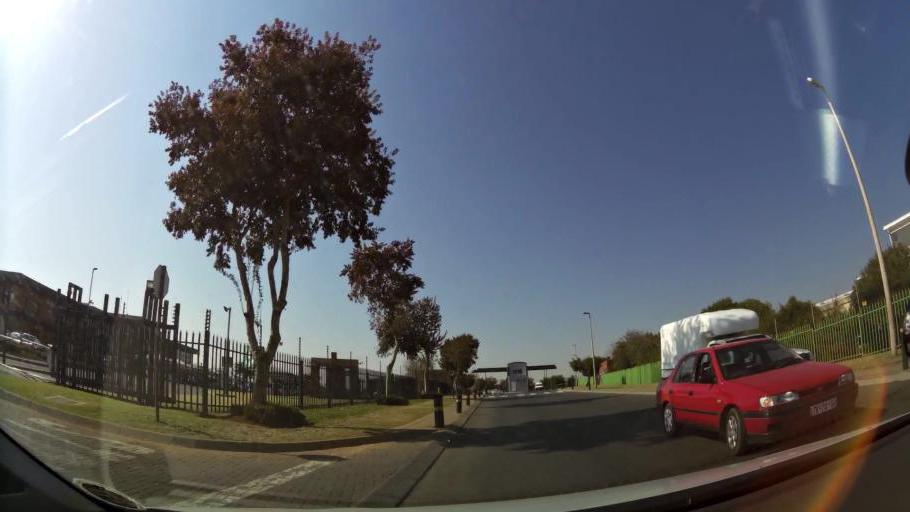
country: ZA
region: Gauteng
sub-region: City of Johannesburg Metropolitan Municipality
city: Modderfontein
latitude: -26.1081
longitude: 28.1345
